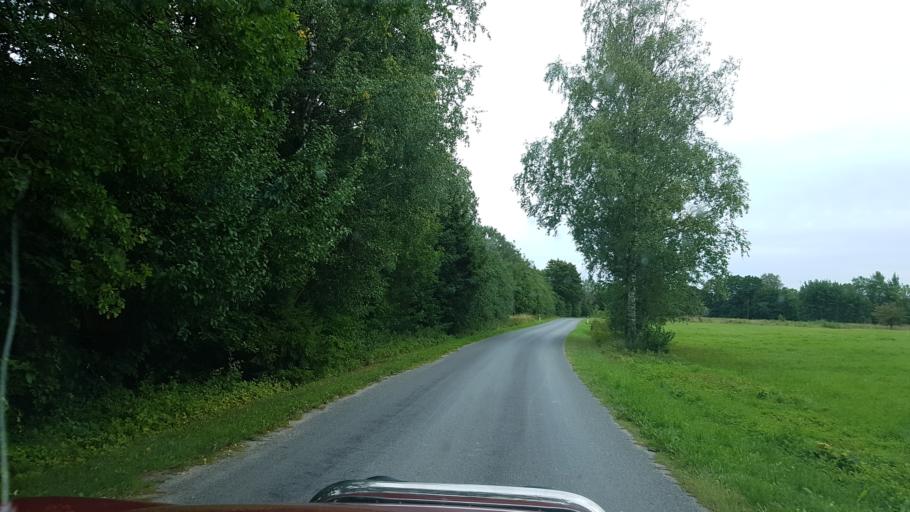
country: EE
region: Laeaene
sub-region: Ridala Parish
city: Uuemoisa
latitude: 59.0174
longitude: 23.7195
